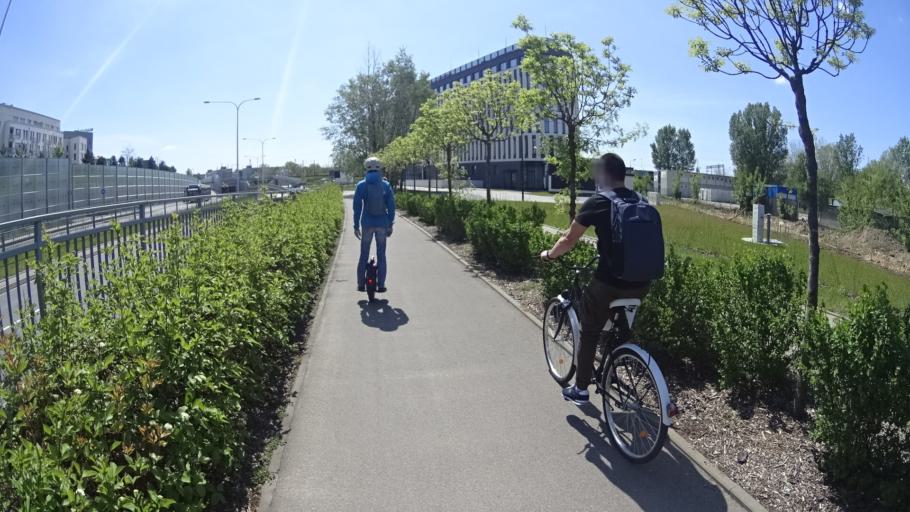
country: PL
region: Masovian Voivodeship
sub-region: Warszawa
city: Ursus
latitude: 52.2069
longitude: 20.8916
